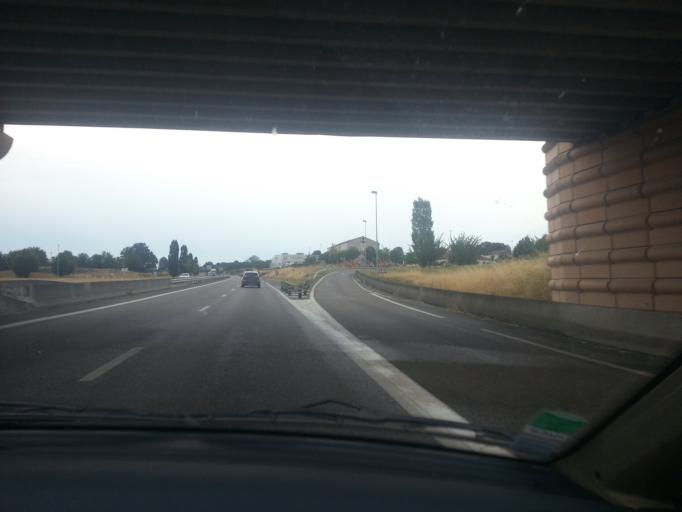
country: FR
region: Bourgogne
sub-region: Departement de Saone-et-Loire
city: Paray-le-Monial
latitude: 46.4688
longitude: 4.1162
